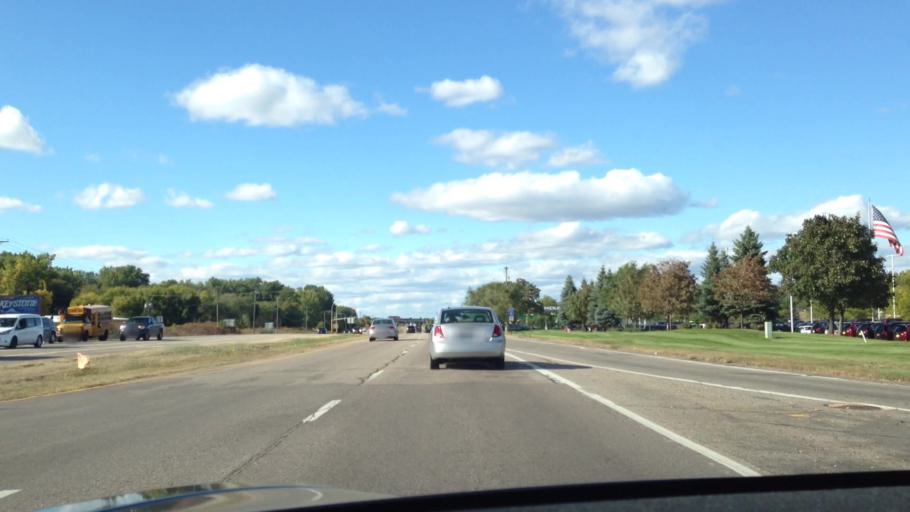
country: US
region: Minnesota
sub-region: Hennepin County
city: Brooklyn Park
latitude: 45.0947
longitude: -93.3841
